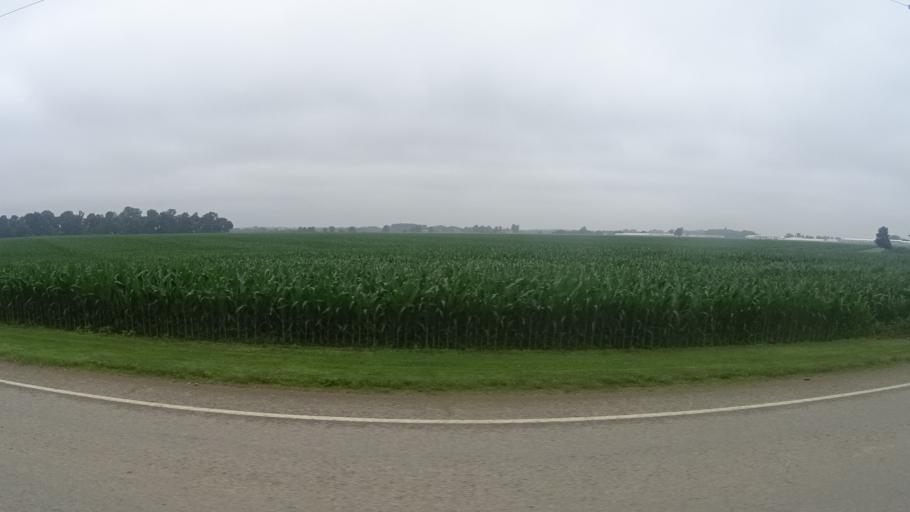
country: US
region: Ohio
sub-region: Erie County
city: Milan
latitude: 41.3464
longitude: -82.6108
